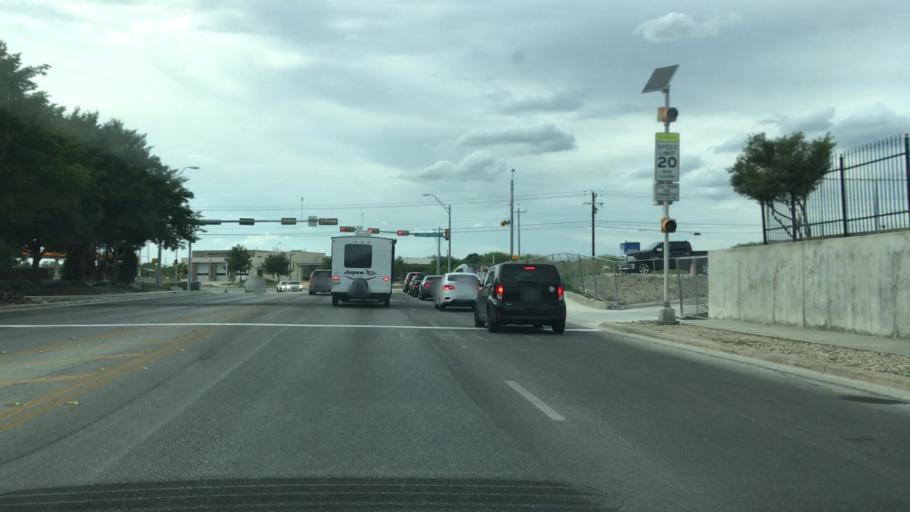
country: US
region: Texas
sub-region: Guadalupe County
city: Northcliff
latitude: 29.5936
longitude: -98.2512
